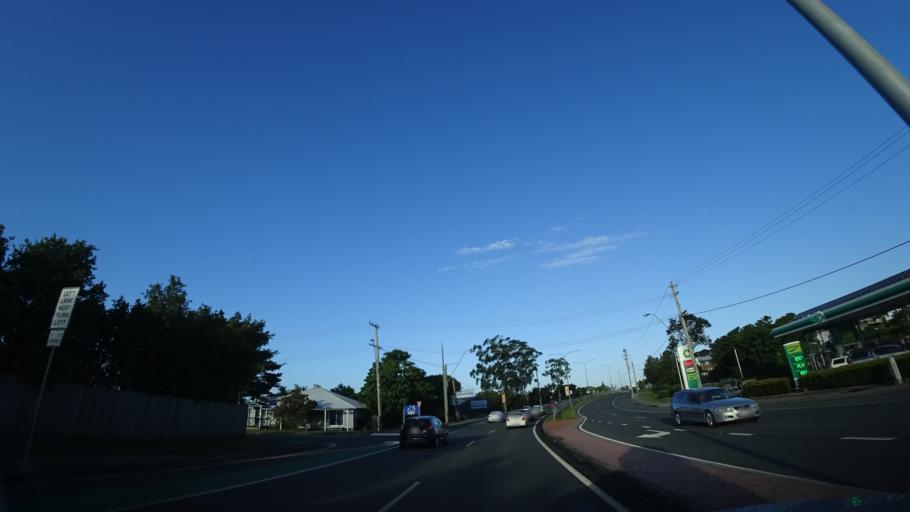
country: AU
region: Queensland
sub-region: Sunshine Coast
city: Buderim
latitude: -26.6554
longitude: 153.0730
